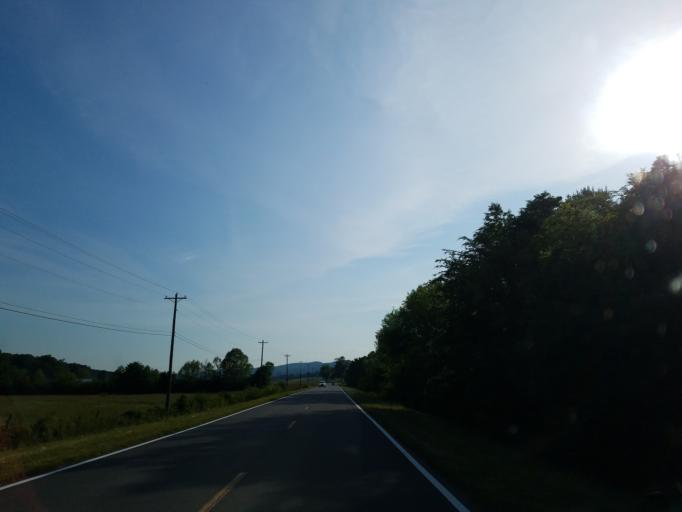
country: US
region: Georgia
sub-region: Chattooga County
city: Trion
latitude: 34.5192
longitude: -85.2250
